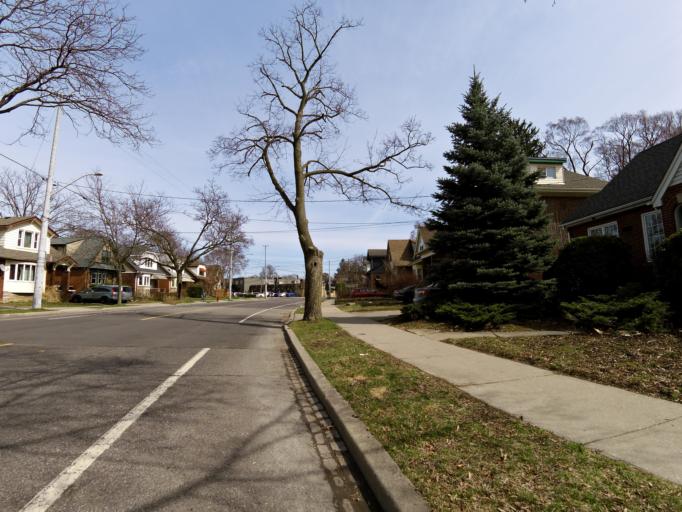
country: CA
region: Ontario
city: Hamilton
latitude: 43.2619
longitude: -79.9087
